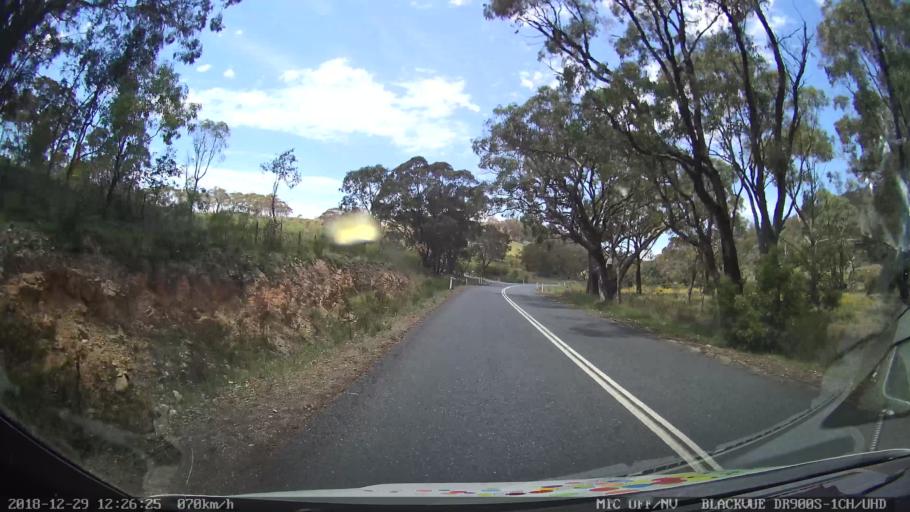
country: AU
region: New South Wales
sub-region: Queanbeyan
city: Queanbeyan
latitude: -35.4653
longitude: 149.2235
